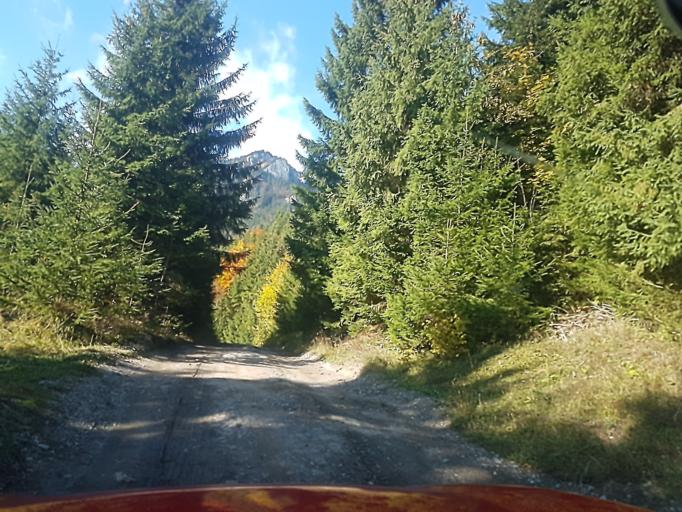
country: SK
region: Zilinsky
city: Ruzomberok
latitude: 49.1320
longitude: 19.3546
